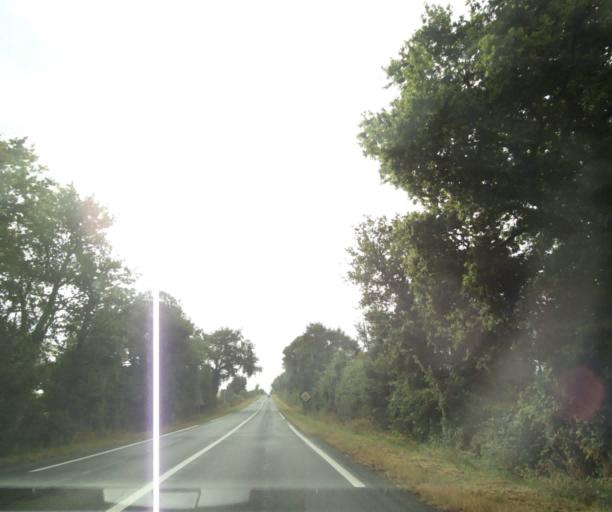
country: FR
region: Pays de la Loire
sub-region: Departement de la Vendee
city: Avrille
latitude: 46.4617
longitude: -1.4535
